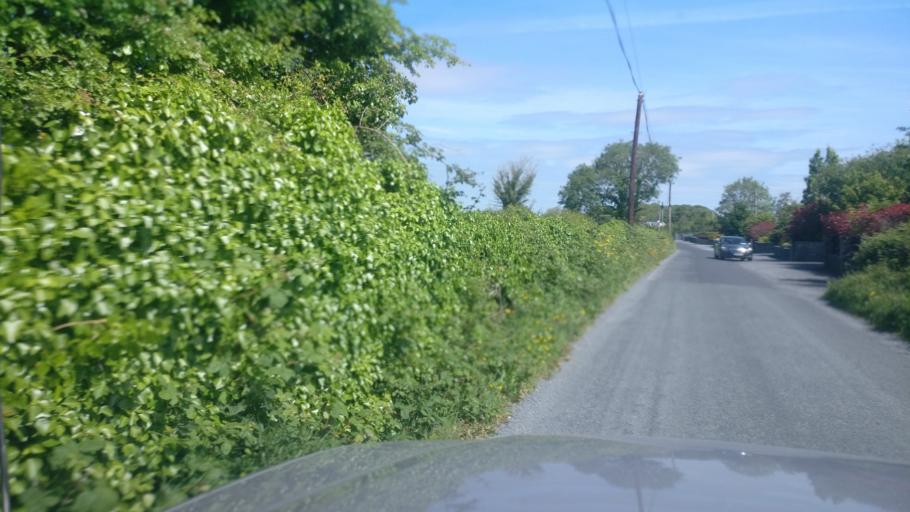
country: IE
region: Connaught
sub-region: County Galway
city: Gort
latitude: 53.0821
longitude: -8.8020
